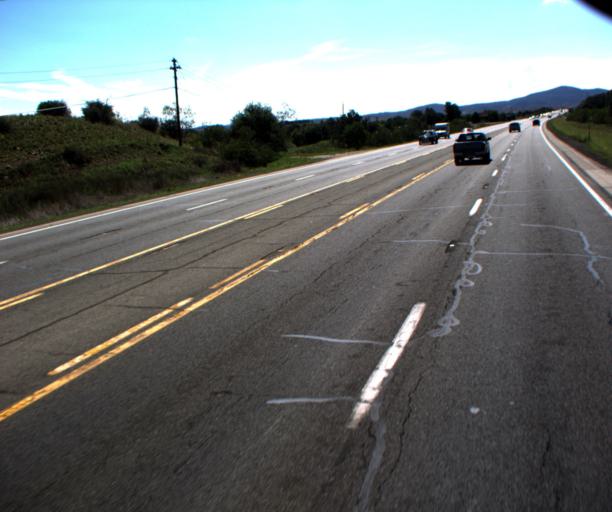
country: US
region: Arizona
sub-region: Yavapai County
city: Dewey-Humboldt
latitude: 34.5707
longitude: -112.2739
